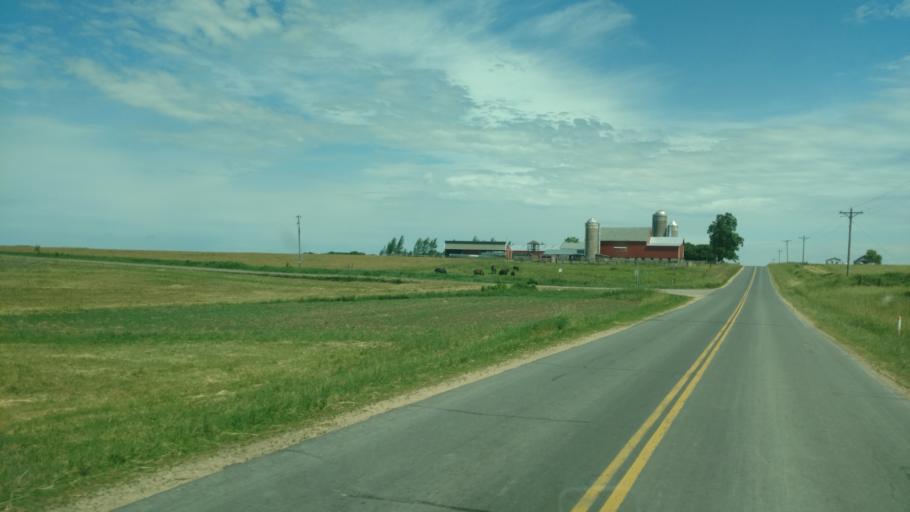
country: US
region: Wisconsin
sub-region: Vernon County
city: Hillsboro
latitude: 43.7578
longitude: -90.4331
